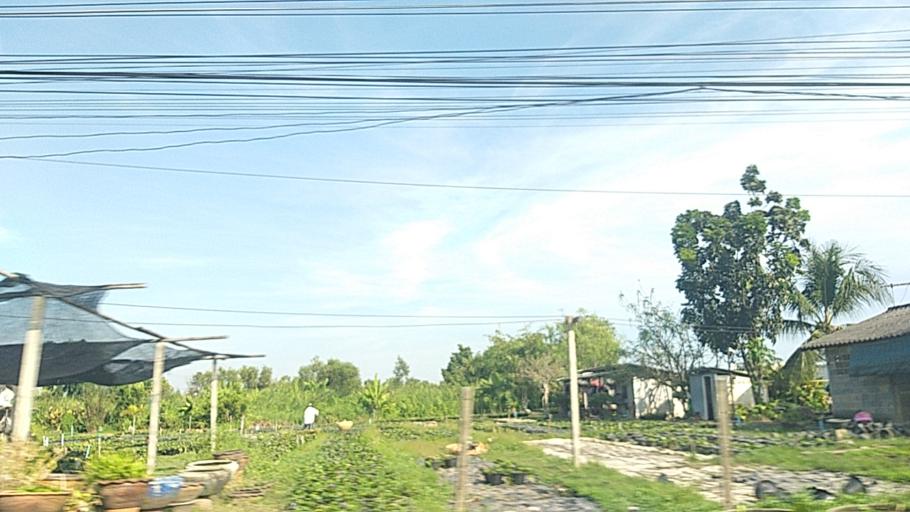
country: TH
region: Pathum Thani
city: Thanyaburi
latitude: 13.9900
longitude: 100.7300
